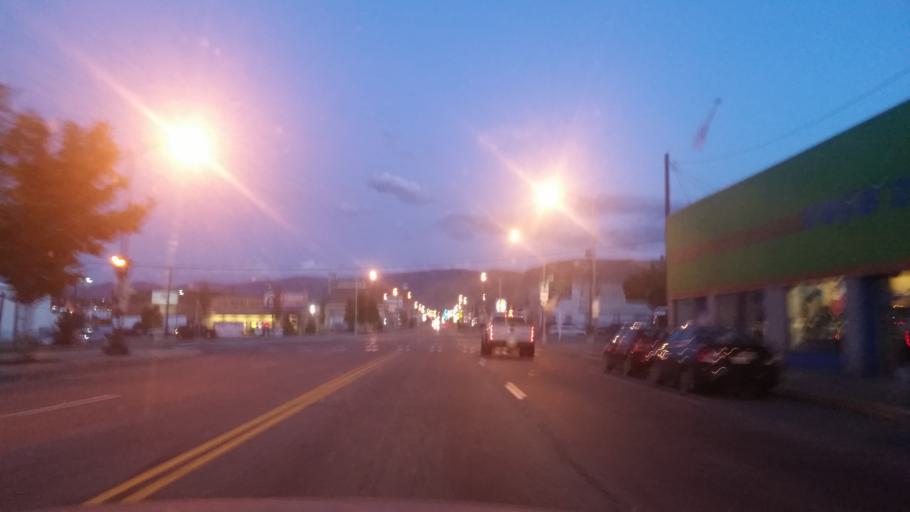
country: US
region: Washington
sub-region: Chelan County
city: Wenatchee
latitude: 47.4201
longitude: -120.3078
